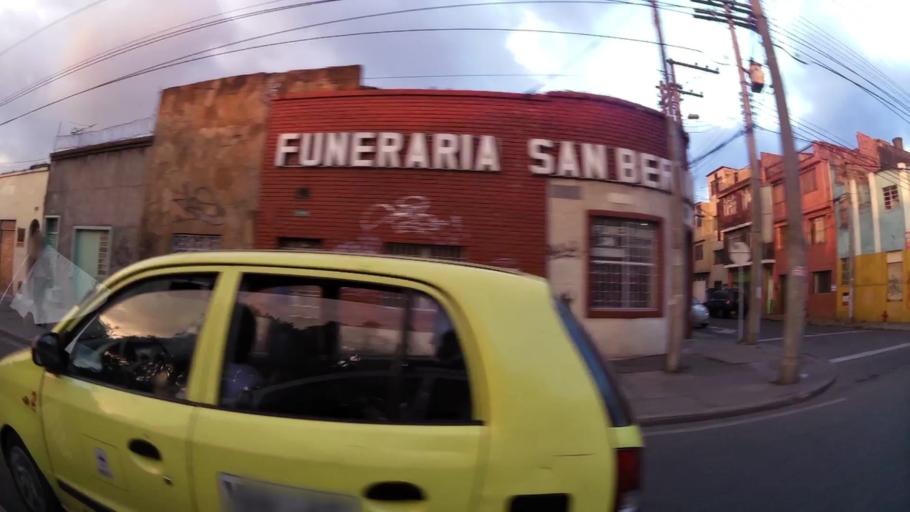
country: CO
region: Bogota D.C.
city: Bogota
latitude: 4.5910
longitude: -74.0874
